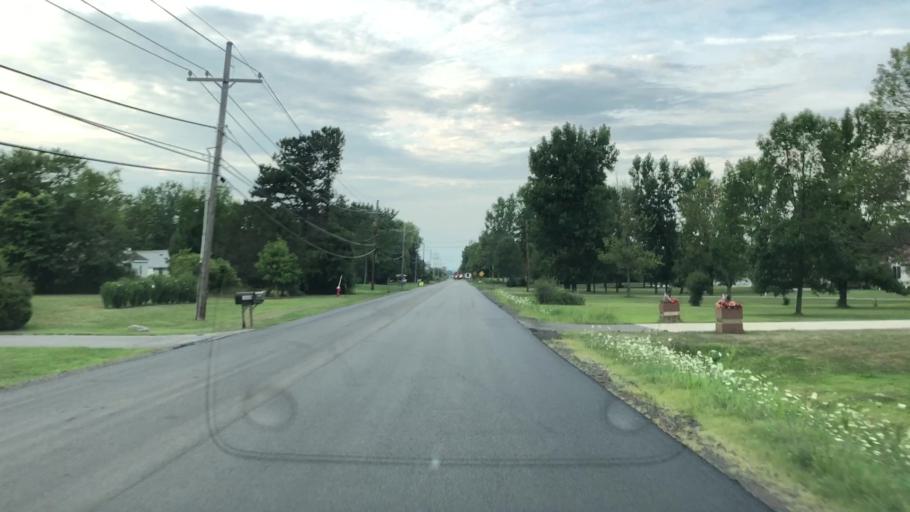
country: US
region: New York
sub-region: Erie County
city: Elma Center
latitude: 42.8189
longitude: -78.6059
